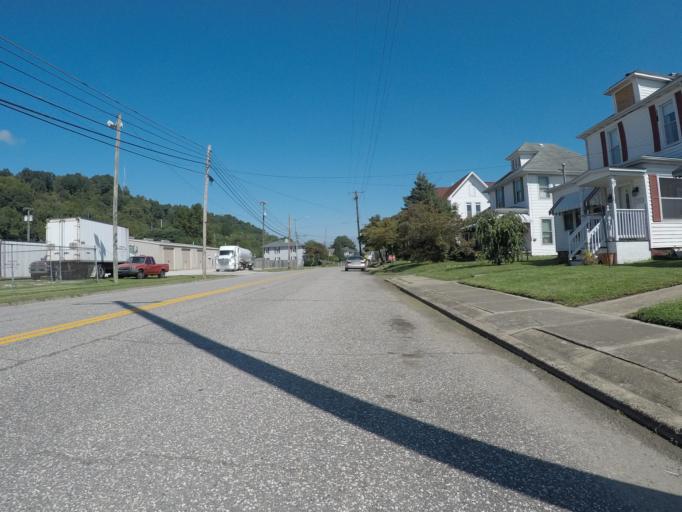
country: US
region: Kentucky
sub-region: Boyd County
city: Catlettsburg
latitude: 38.4063
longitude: -82.5989
